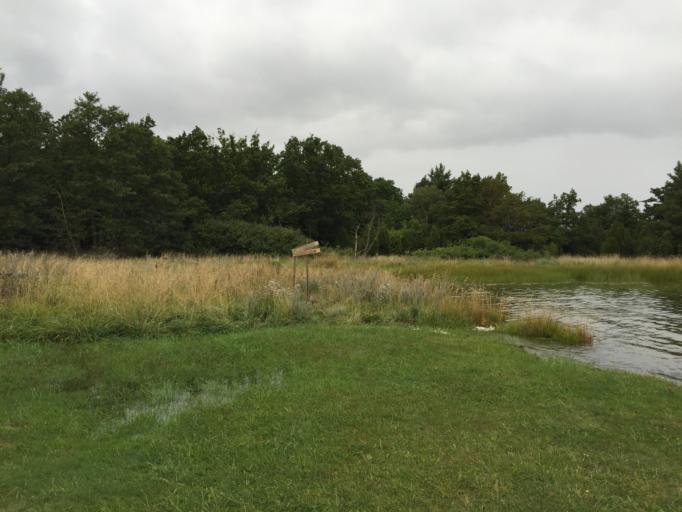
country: SE
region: Kalmar
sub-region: Monsteras Kommun
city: Moensteras
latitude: 57.0465
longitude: 16.5799
